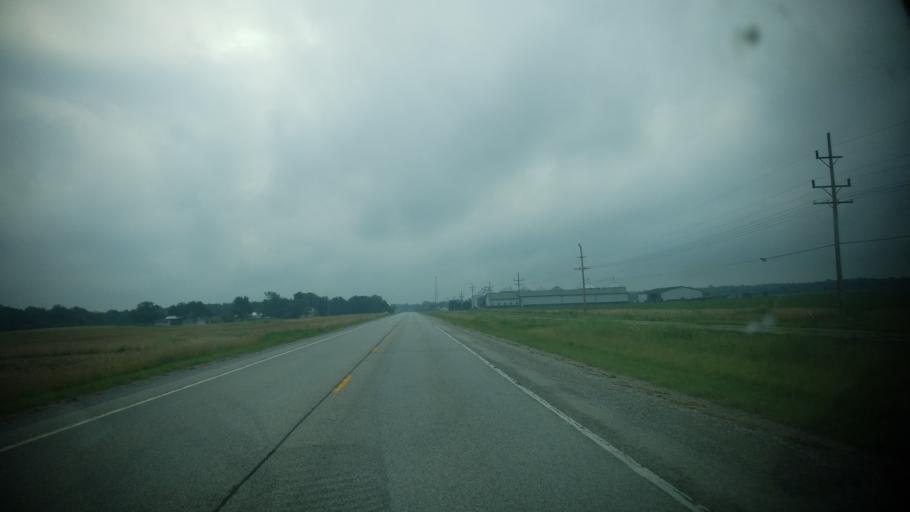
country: US
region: Illinois
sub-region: Clay County
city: Flora
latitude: 38.6777
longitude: -88.3776
